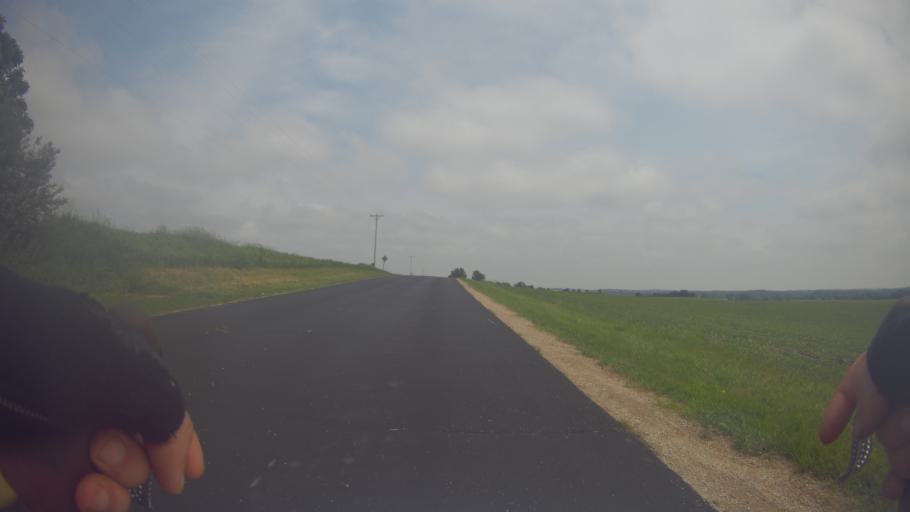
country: US
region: Wisconsin
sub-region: Rock County
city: Edgerton
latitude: 42.9073
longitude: -89.0426
